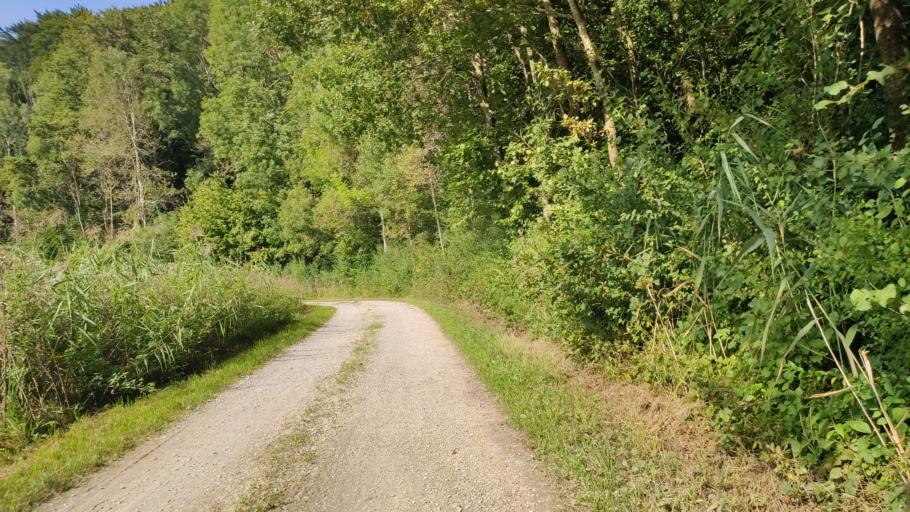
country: DE
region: Bavaria
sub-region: Upper Bavaria
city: Kaufering
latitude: 48.1191
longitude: 10.8605
